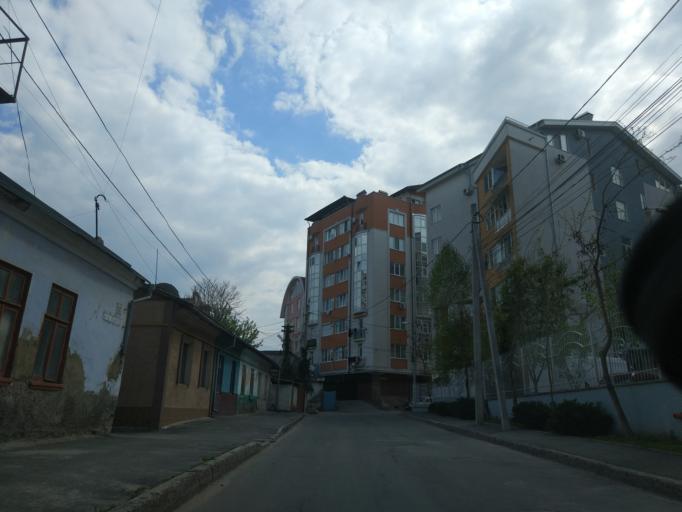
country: MD
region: Chisinau
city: Chisinau
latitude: 47.0276
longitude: 28.8455
